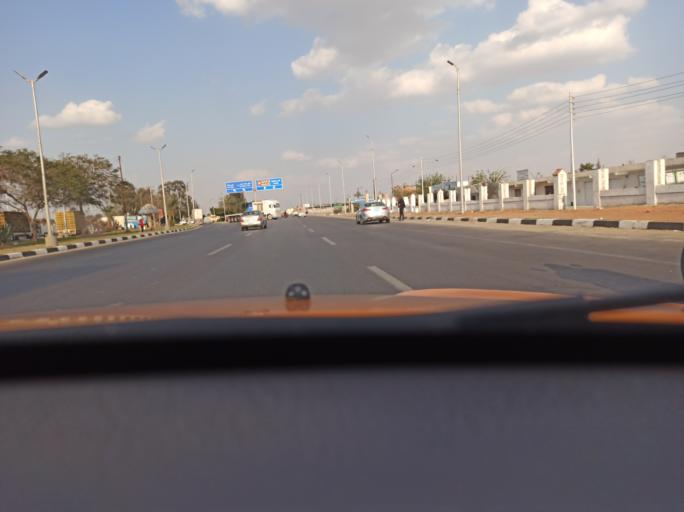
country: EG
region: Al Isma'iliyah
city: Ismailia
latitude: 30.6194
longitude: 32.2419
